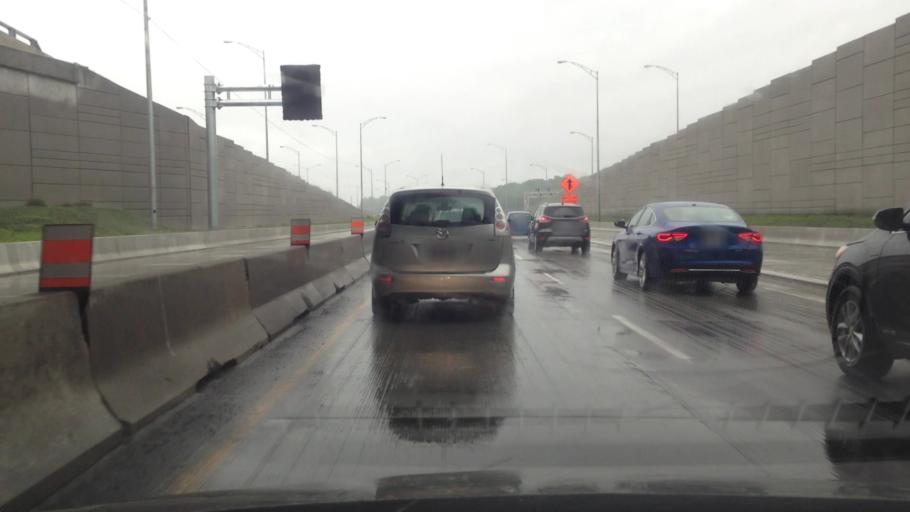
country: CA
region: Quebec
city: Saint-Raymond
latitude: 45.4650
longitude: -73.6069
